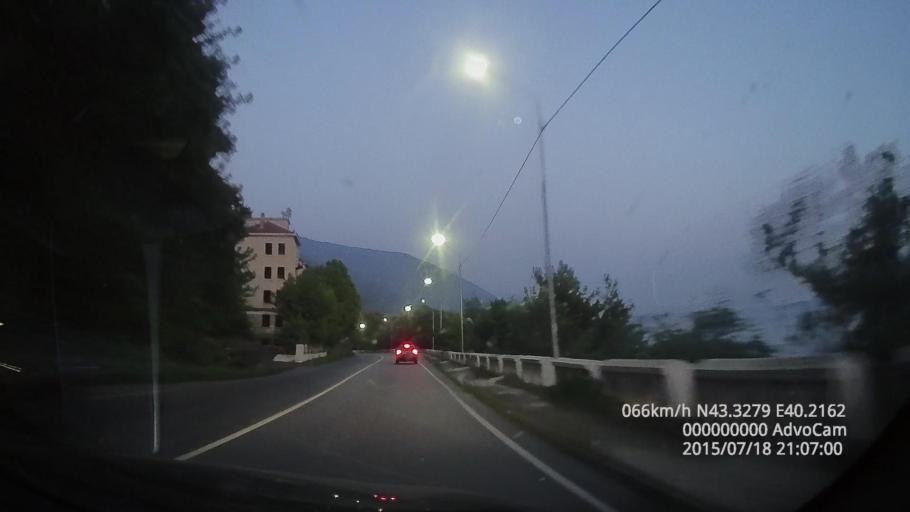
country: GE
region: Abkhazia
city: Gagra
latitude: 43.3278
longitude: 40.2166
